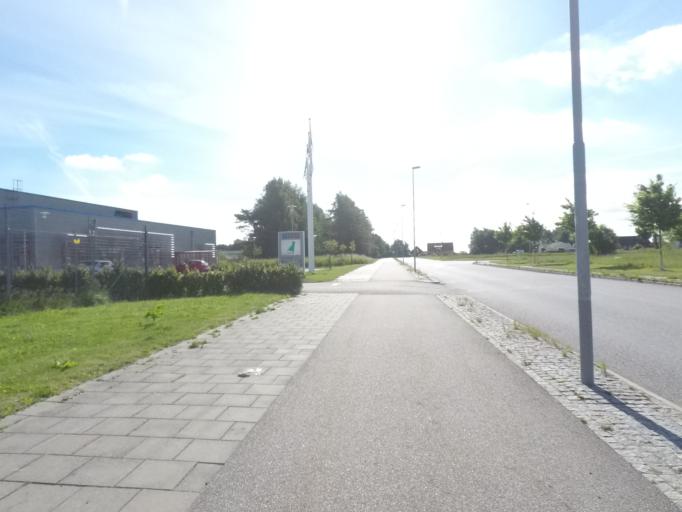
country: SE
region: Skane
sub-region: Burlovs Kommun
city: Arloev
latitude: 55.5960
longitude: 13.1000
